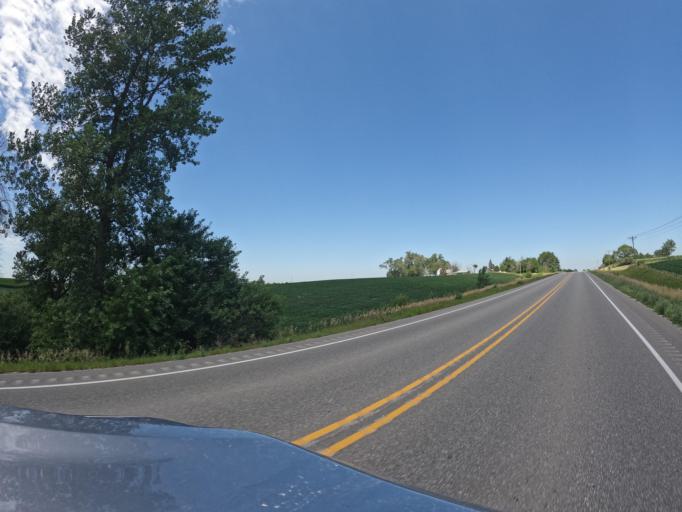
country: US
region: Iowa
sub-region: Keokuk County
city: Sigourney
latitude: 41.4361
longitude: -92.3549
